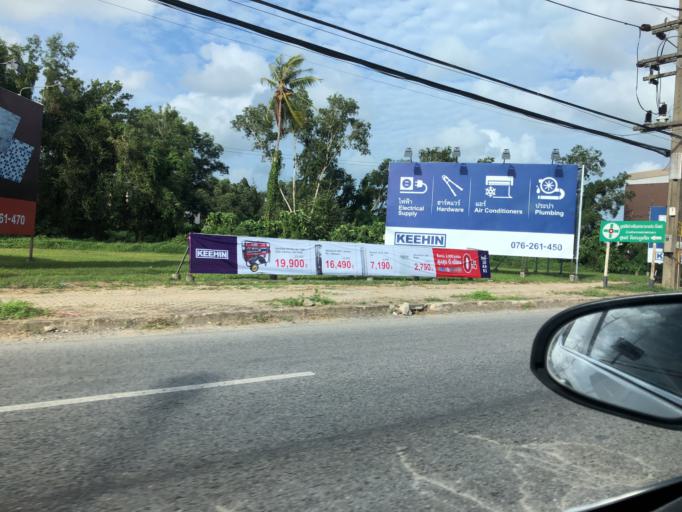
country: TH
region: Phuket
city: Ban Ko Kaeo
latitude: 7.9691
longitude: 98.3711
